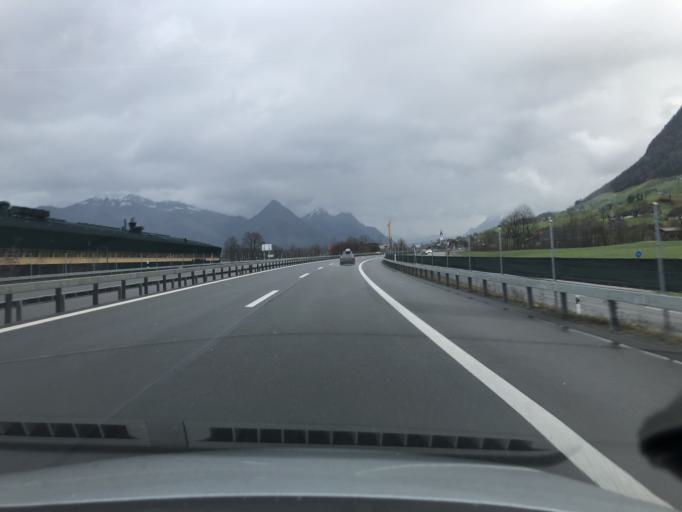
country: CH
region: Nidwalden
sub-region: Nidwalden
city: Ennetburgen
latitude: 46.9691
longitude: 8.3979
